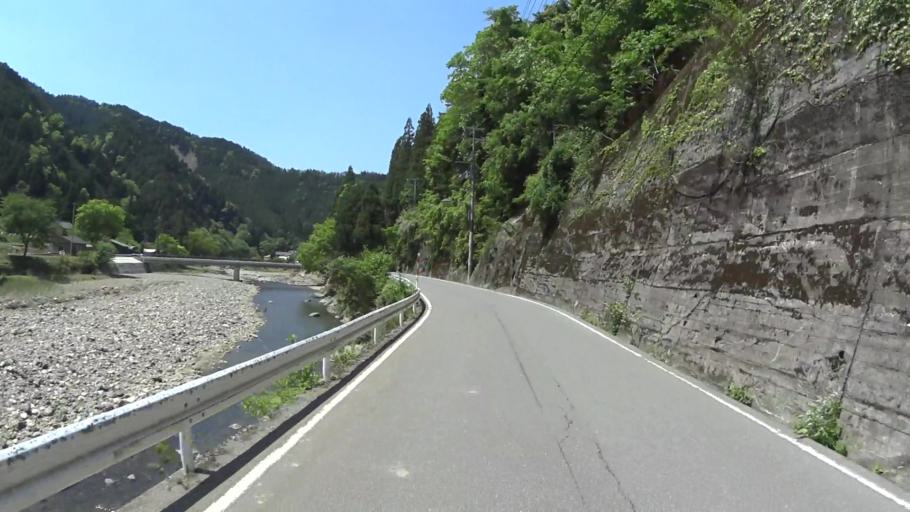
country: JP
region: Kyoto
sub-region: Kyoto-shi
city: Kamigyo-ku
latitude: 35.2052
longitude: 135.7295
